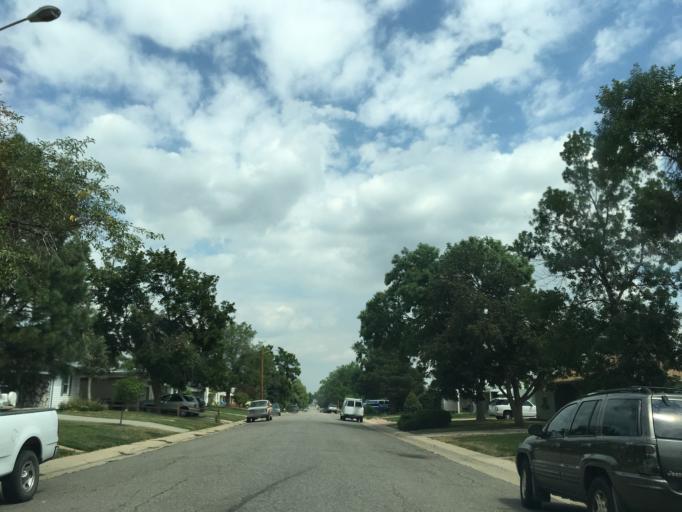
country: US
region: Colorado
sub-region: Arapahoe County
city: Sheridan
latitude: 39.6654
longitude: -105.0289
